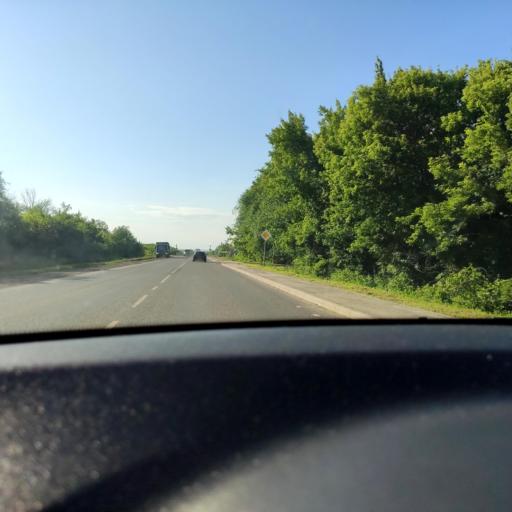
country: RU
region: Samara
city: Samara
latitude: 53.0836
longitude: 50.1604
